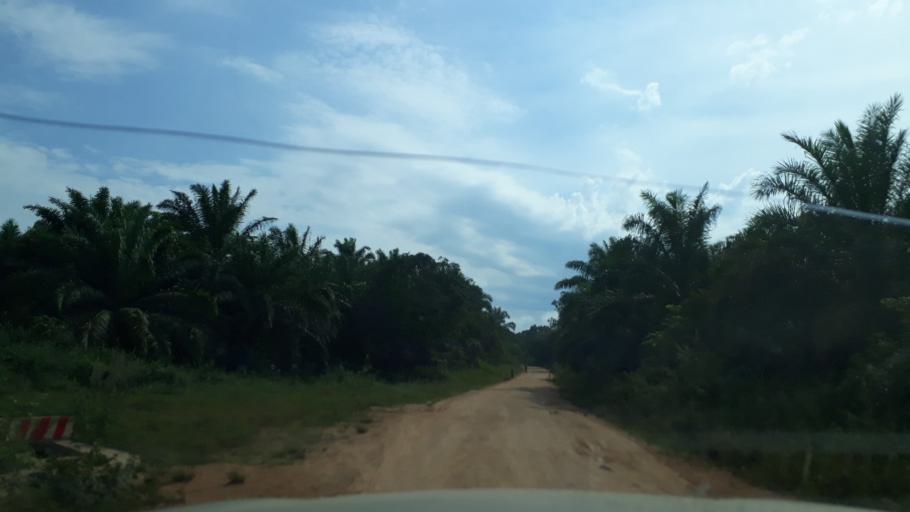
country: CD
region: Eastern Province
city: Bunia
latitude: 1.3906
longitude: 29.7969
